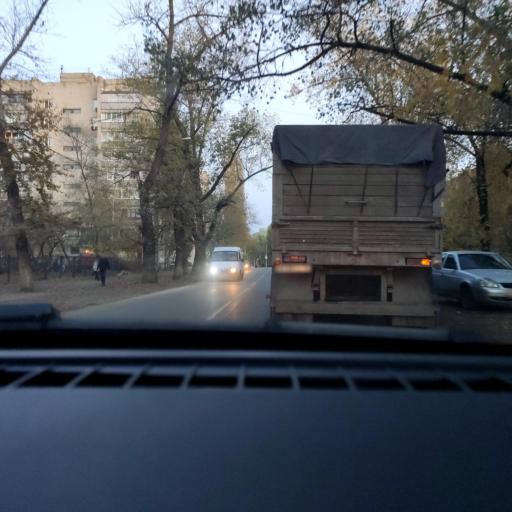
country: RU
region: Voronezj
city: Voronezh
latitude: 51.6406
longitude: 39.2704
